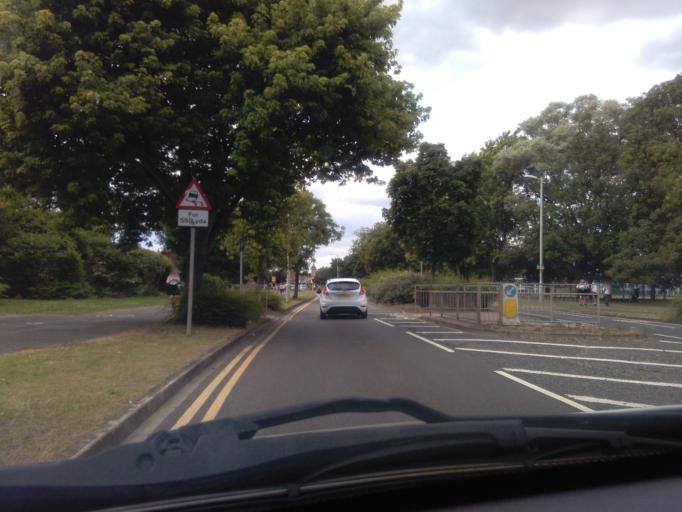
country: GB
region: England
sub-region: Bedford
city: Bedford
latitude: 52.1430
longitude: -0.4443
